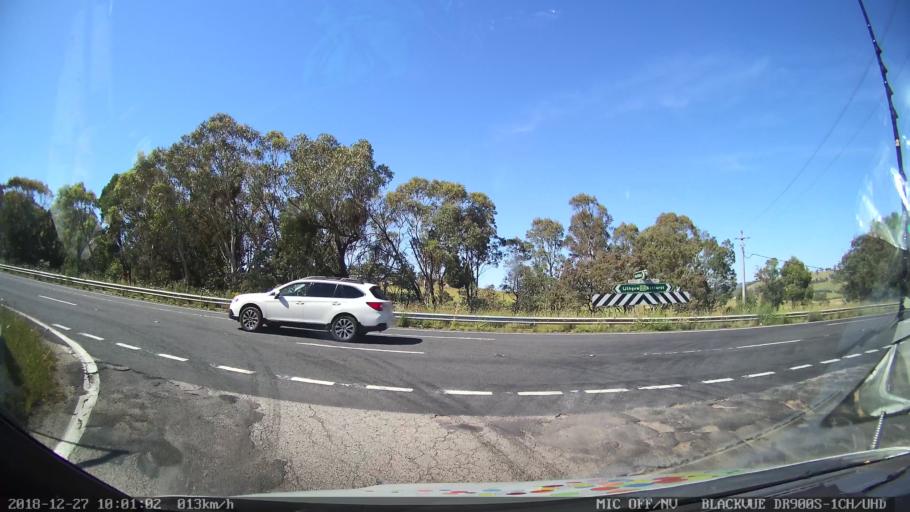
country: AU
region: New South Wales
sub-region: Lithgow
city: Portland
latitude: -33.4394
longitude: 149.9367
